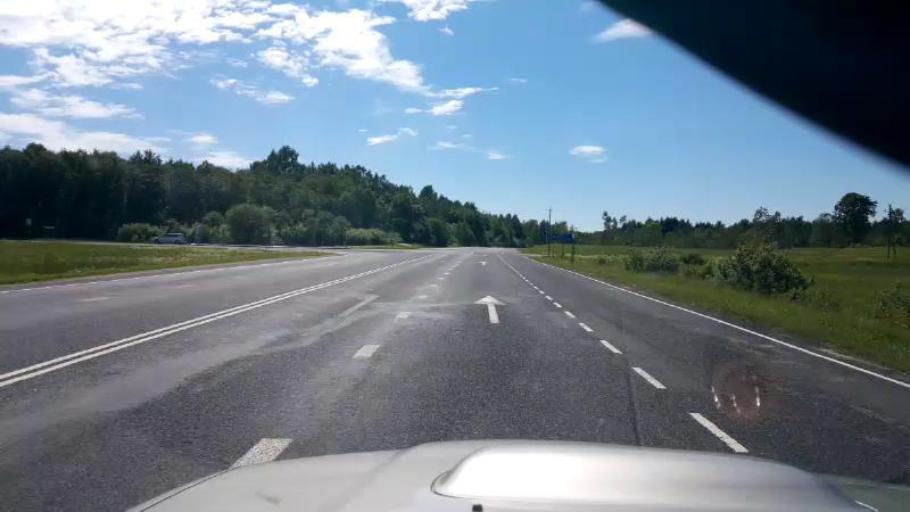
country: EE
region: Jaervamaa
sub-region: Jaerva-Jaani vald
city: Jarva-Jaani
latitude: 59.0489
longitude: 25.8793
